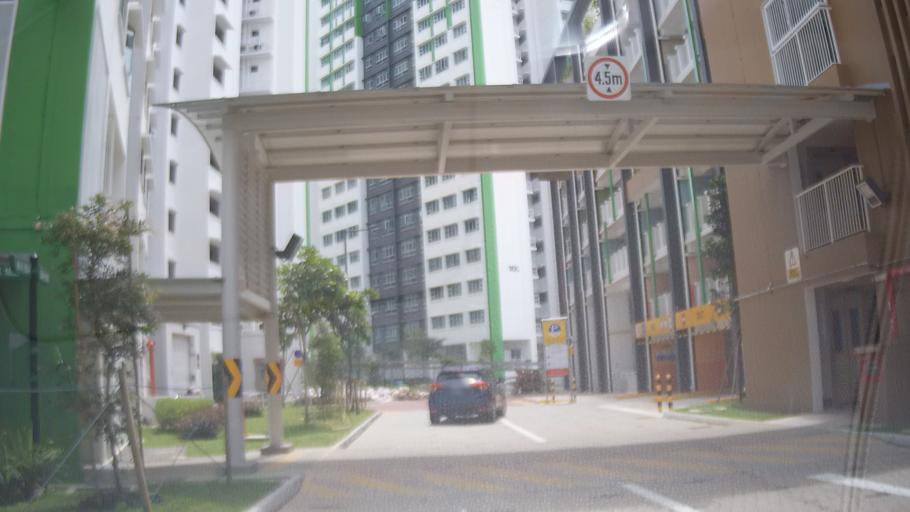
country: MY
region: Johor
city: Johor Bahru
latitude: 1.4357
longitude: 103.7762
